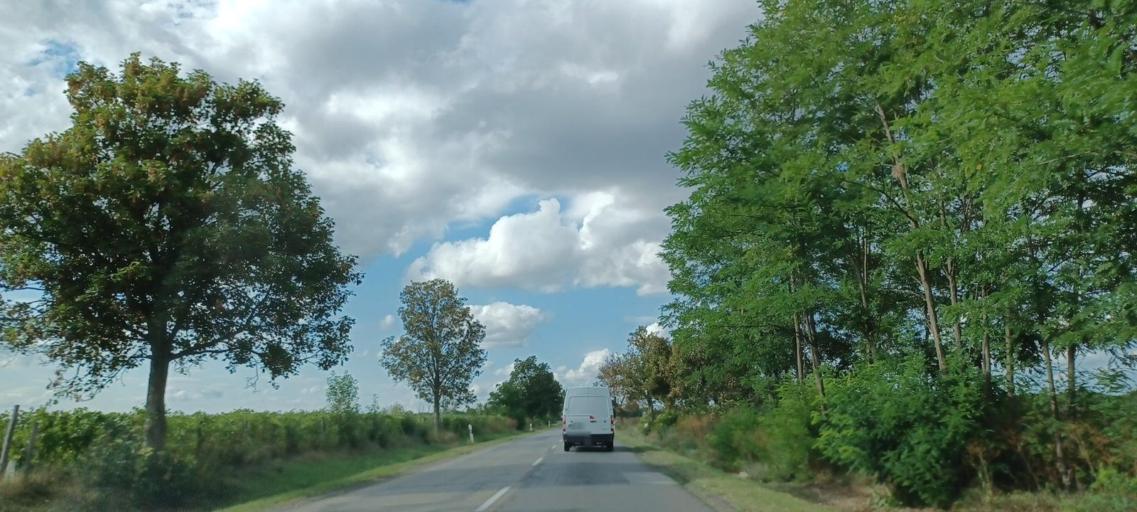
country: HU
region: Tolna
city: Szentgalpuszta
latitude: 46.3925
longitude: 18.6246
